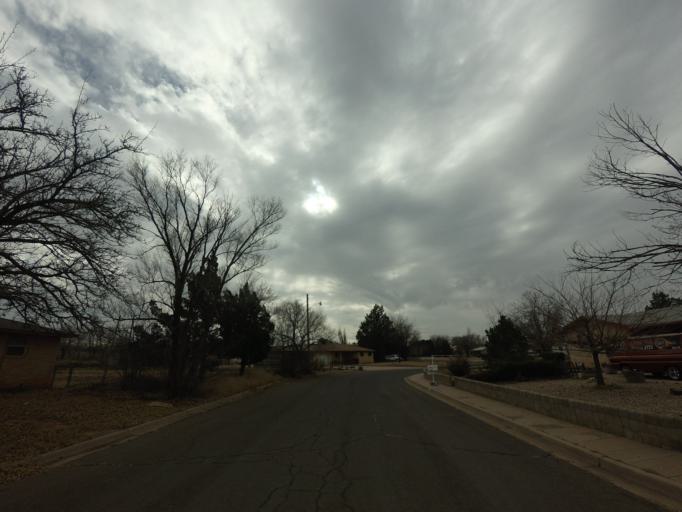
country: US
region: New Mexico
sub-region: Curry County
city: Clovis
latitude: 34.3819
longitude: -103.2005
